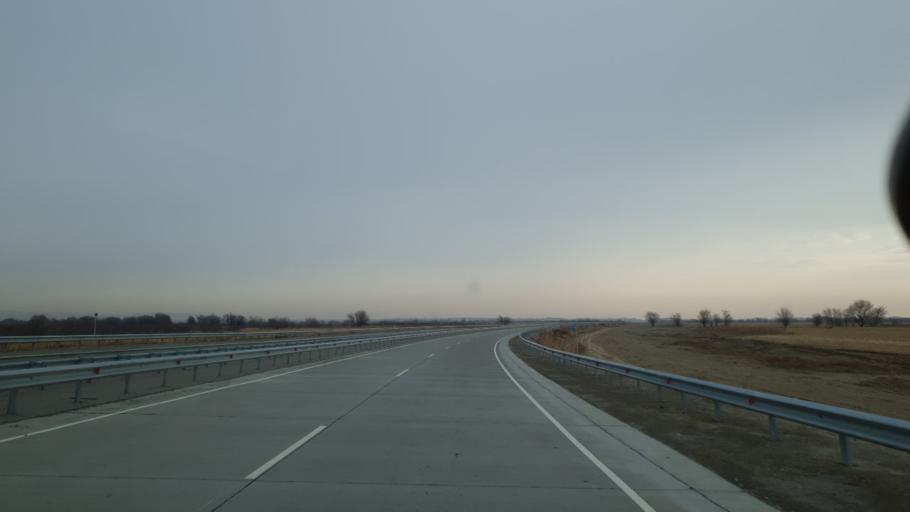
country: KZ
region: Almaty Oblysy
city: Zharkent
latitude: 44.1766
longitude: 80.1670
